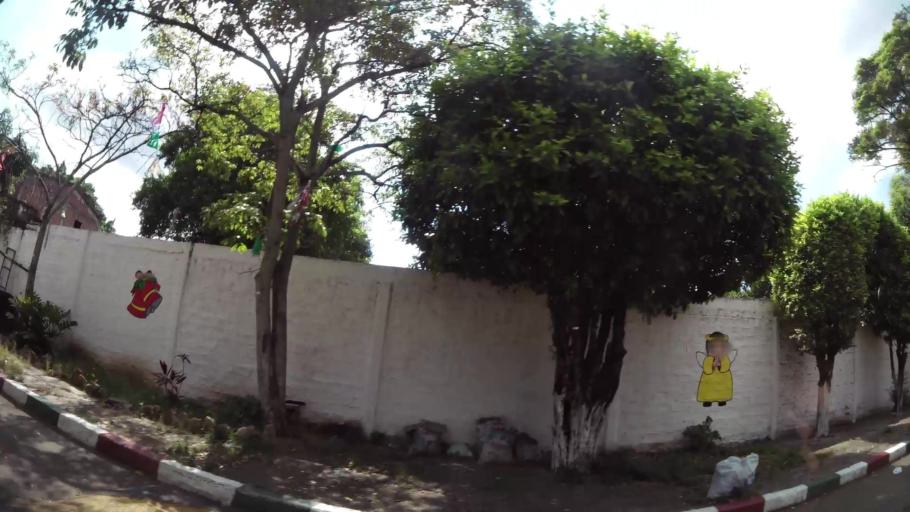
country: CO
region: Valle del Cauca
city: Cali
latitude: 3.4182
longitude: -76.5182
